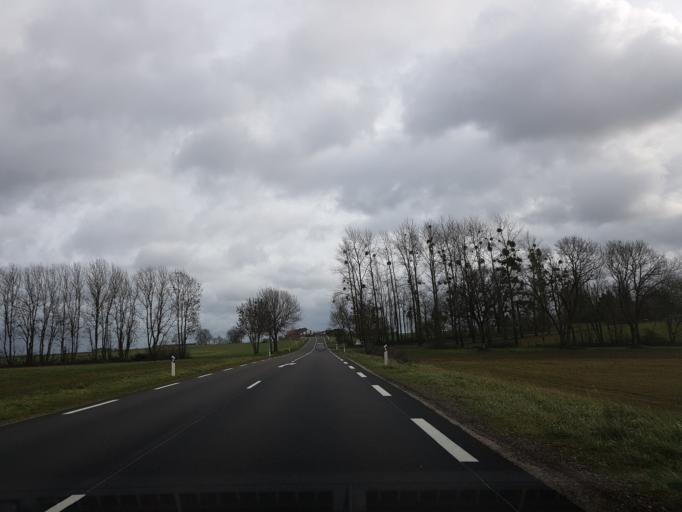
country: FR
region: Champagne-Ardenne
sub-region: Departement de la Haute-Marne
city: Chalindrey
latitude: 47.8515
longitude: 5.4087
